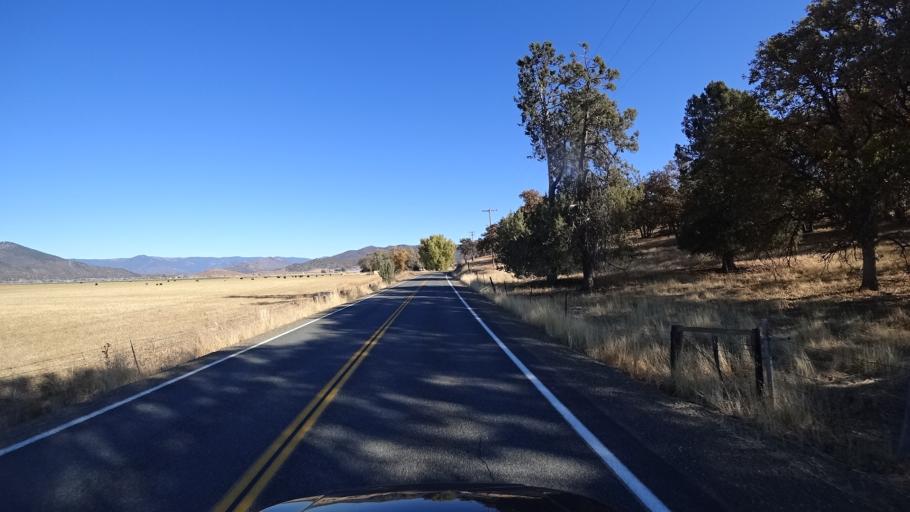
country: US
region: California
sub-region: Siskiyou County
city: Yreka
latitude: 41.5563
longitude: -122.8278
